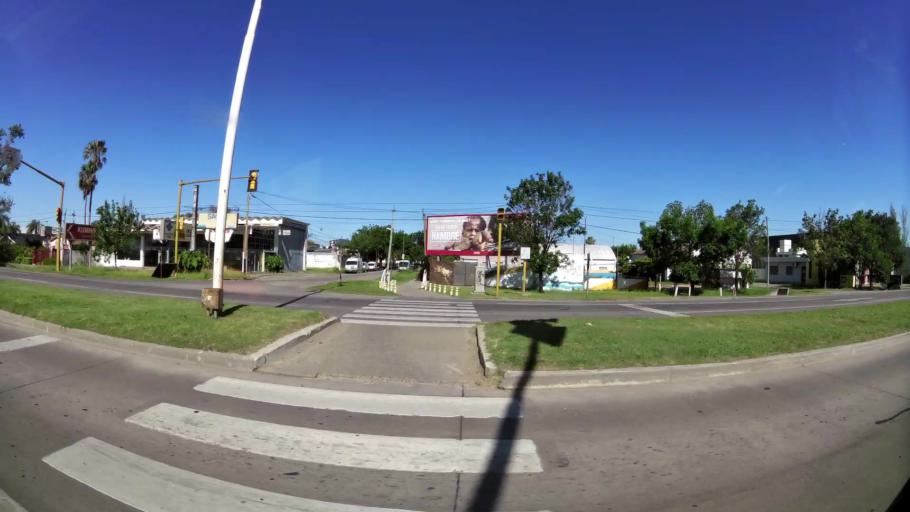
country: AR
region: Santa Fe
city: Rafaela
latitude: -31.2478
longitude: -61.5062
